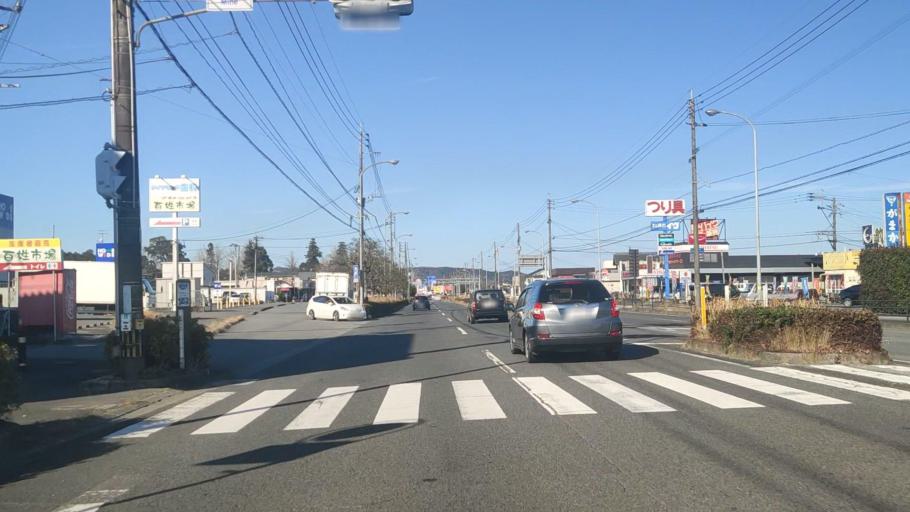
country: JP
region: Oita
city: Oita
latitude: 33.1439
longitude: 131.6579
